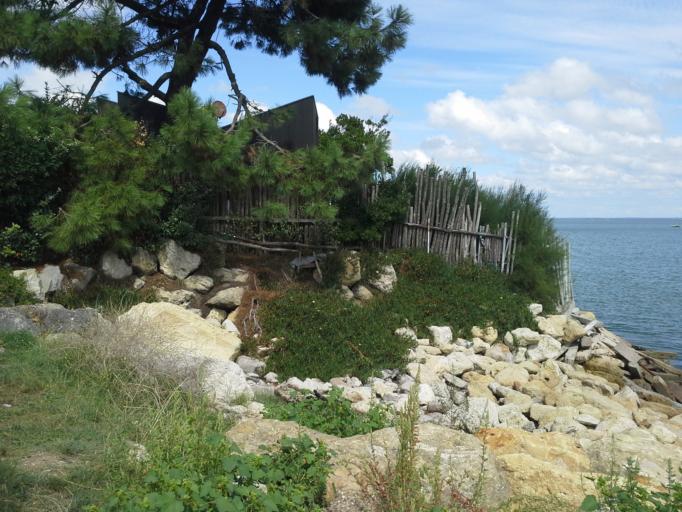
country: FR
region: Aquitaine
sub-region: Departement de la Gironde
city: Arcachon
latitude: 44.6290
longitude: -1.2430
